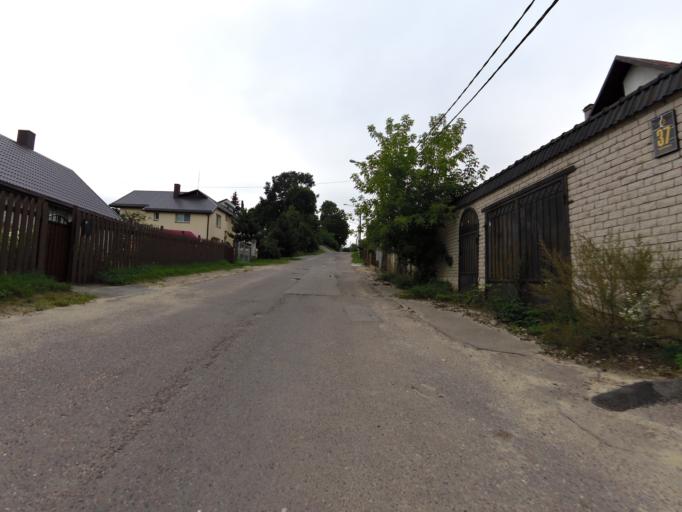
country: LT
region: Vilnius County
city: Rasos
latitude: 54.6628
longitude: 25.2922
